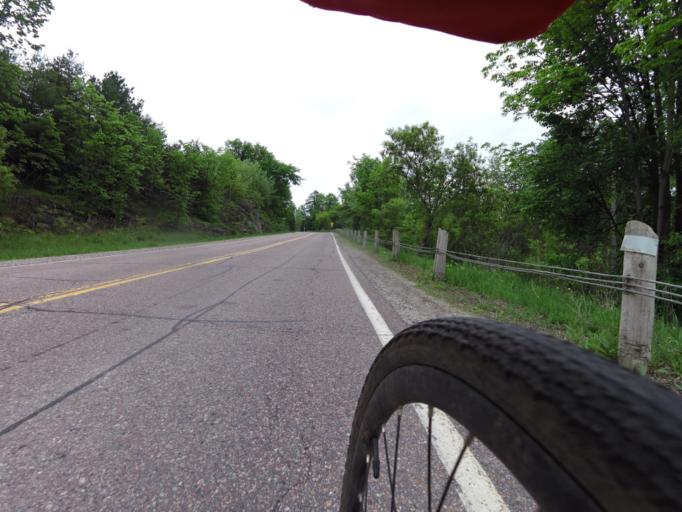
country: CA
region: Ontario
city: Renfrew
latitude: 45.2986
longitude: -76.7169
